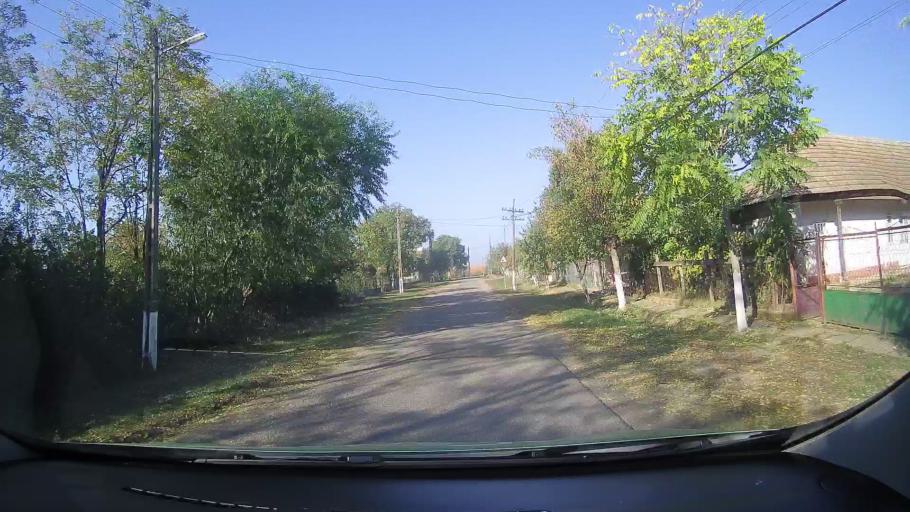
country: RO
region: Satu Mare
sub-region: Comuna Sauca
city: Sauca
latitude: 47.4694
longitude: 22.4958
